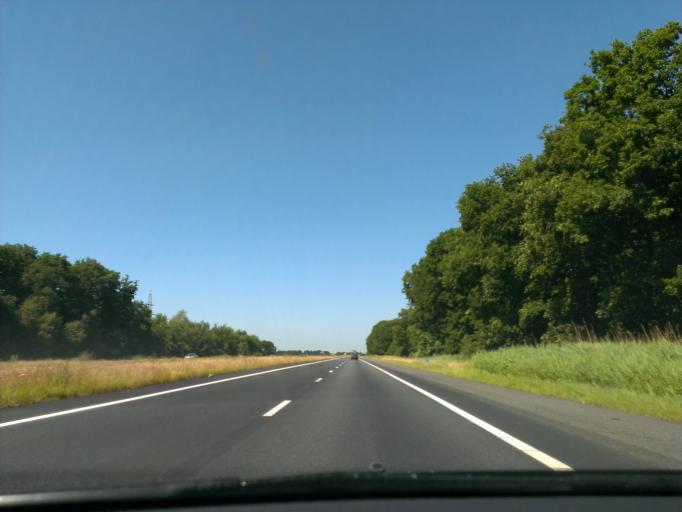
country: NL
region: Drenthe
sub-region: Gemeente Coevorden
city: Dalen
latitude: 52.7238
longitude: 6.6956
